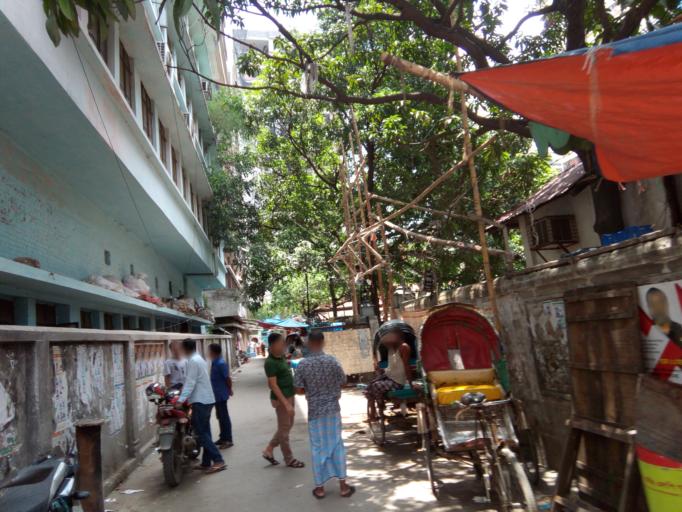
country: BD
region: Dhaka
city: Paltan
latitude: 23.7299
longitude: 90.4177
